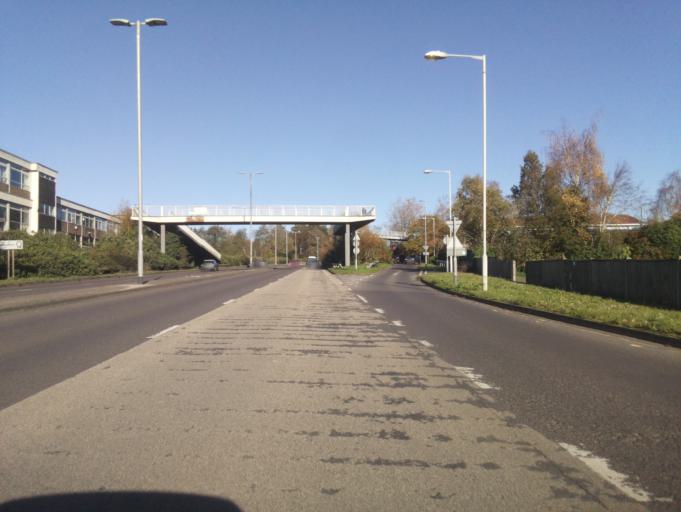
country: GB
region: England
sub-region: Somerset
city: Yeovil
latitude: 50.9408
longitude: -2.6387
